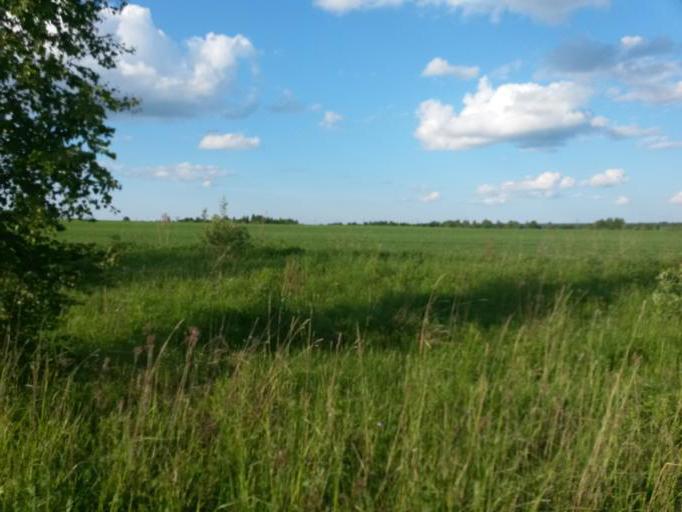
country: RU
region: Jaroslavl
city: Burmakino
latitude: 57.3574
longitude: 40.2022
